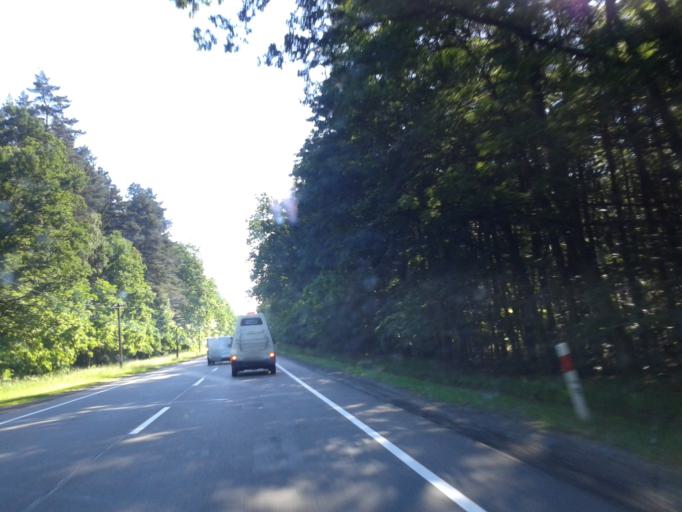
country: PL
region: Pomeranian Voivodeship
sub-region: Powiat chojnicki
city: Czersk
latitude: 53.7842
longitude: 17.9162
